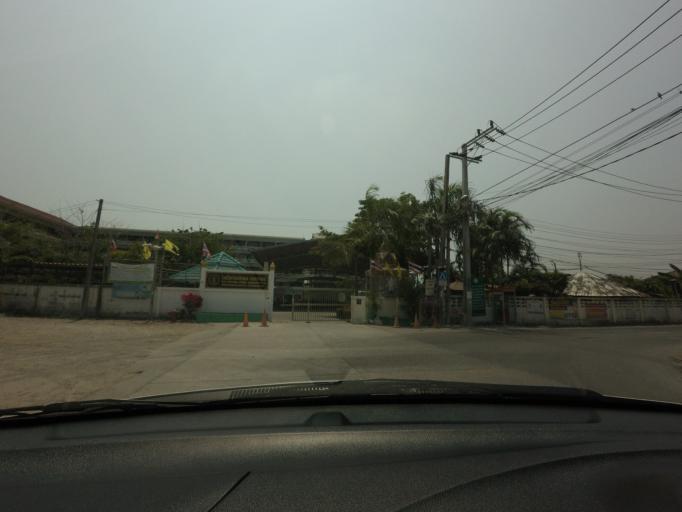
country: TH
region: Bangkok
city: Khlong Sam Wa
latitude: 13.8861
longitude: 100.7093
